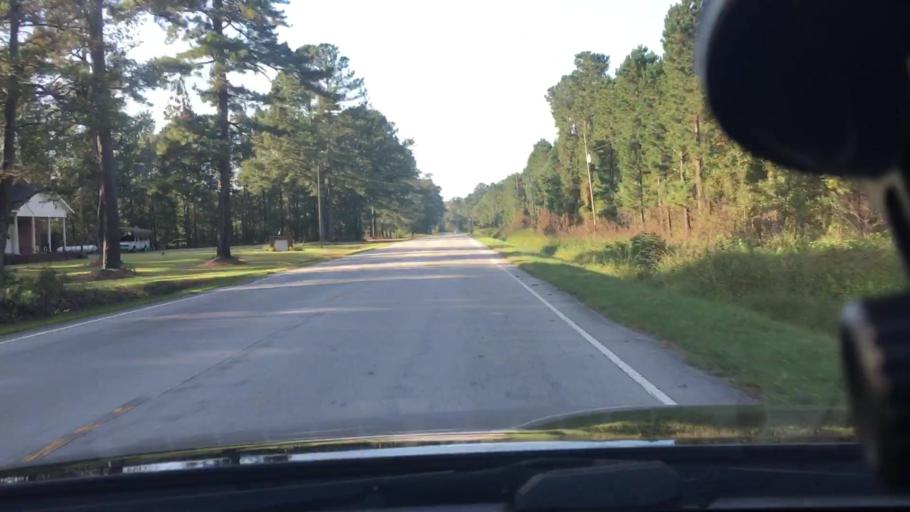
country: US
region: North Carolina
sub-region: Craven County
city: Vanceboro
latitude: 35.4045
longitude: -77.2411
